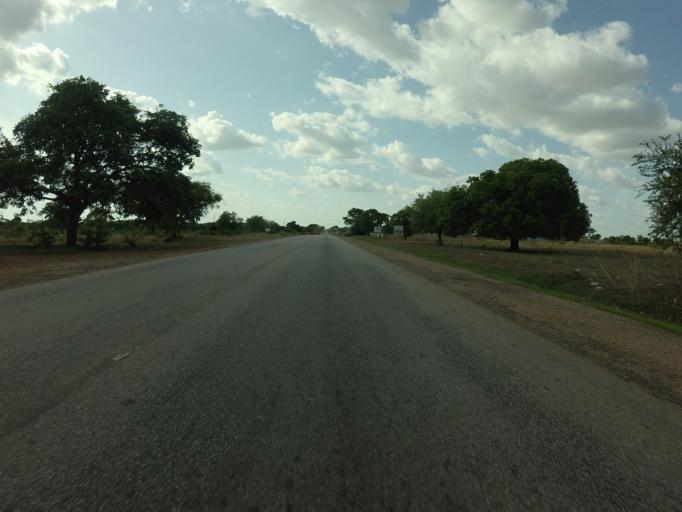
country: GH
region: Upper East
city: Bolgatanga
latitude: 10.6647
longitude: -0.8599
